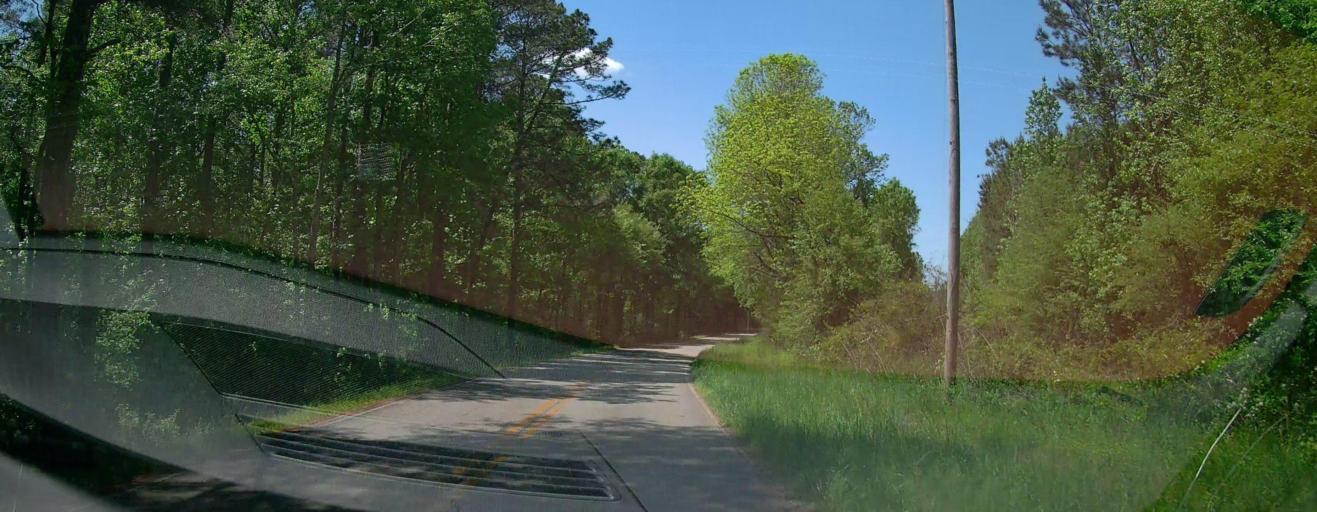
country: US
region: Georgia
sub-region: Jasper County
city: Monticello
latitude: 33.2812
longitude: -83.7101
